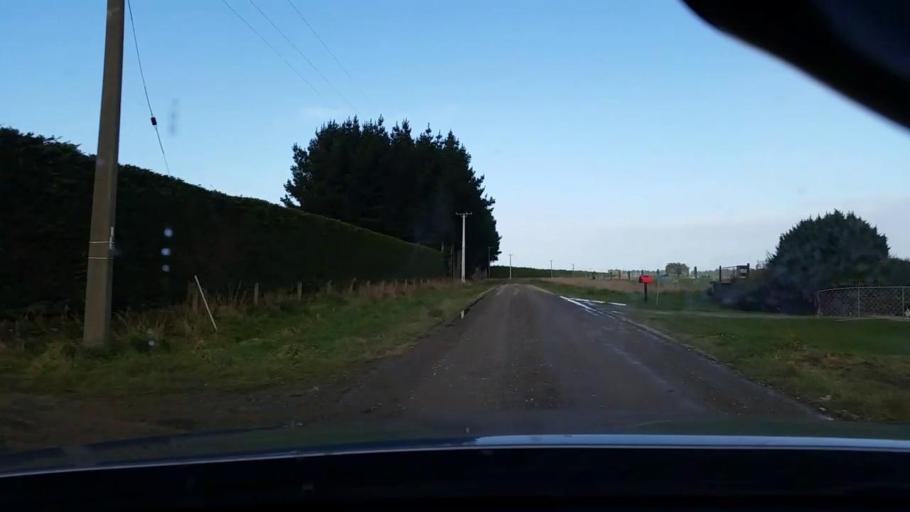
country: NZ
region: Southland
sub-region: Invercargill City
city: Invercargill
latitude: -46.2807
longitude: 168.2940
